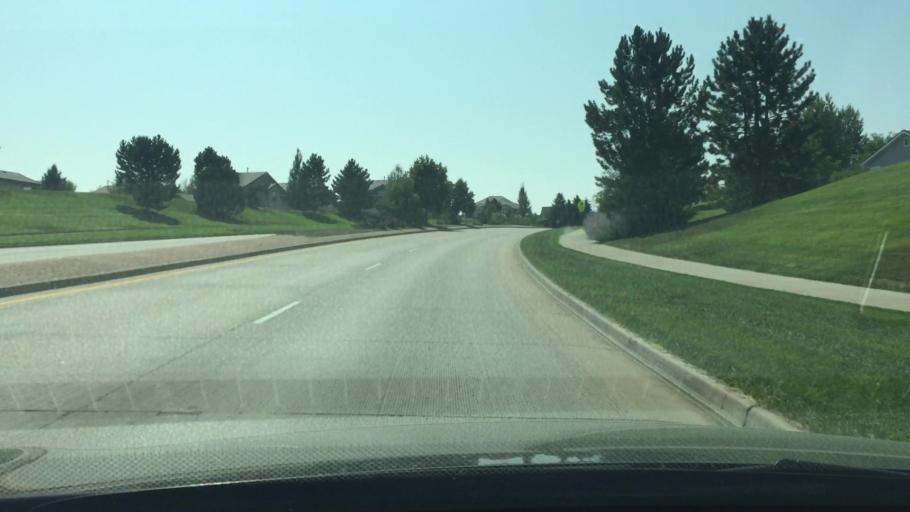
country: US
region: Colorado
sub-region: Arapahoe County
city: Dove Valley
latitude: 39.6044
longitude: -104.7872
